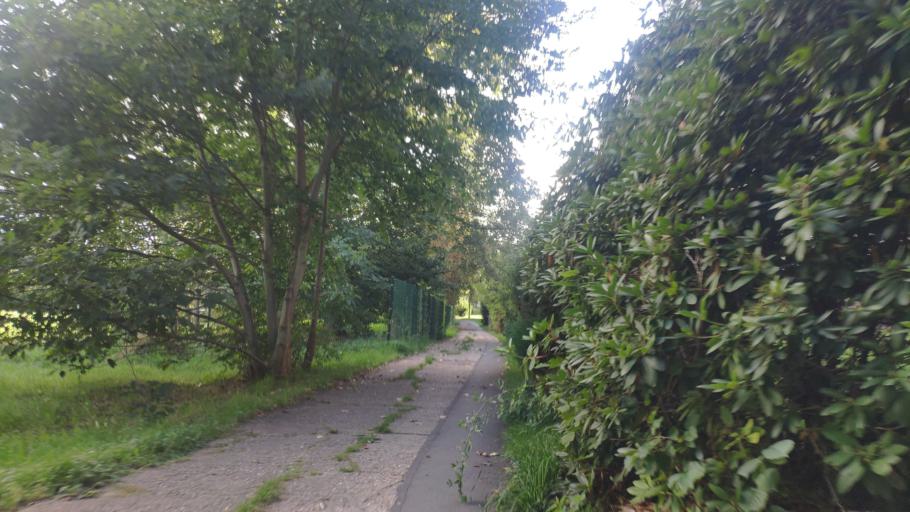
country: DE
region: Saxony
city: Chemnitz
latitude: 50.8088
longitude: 12.8998
